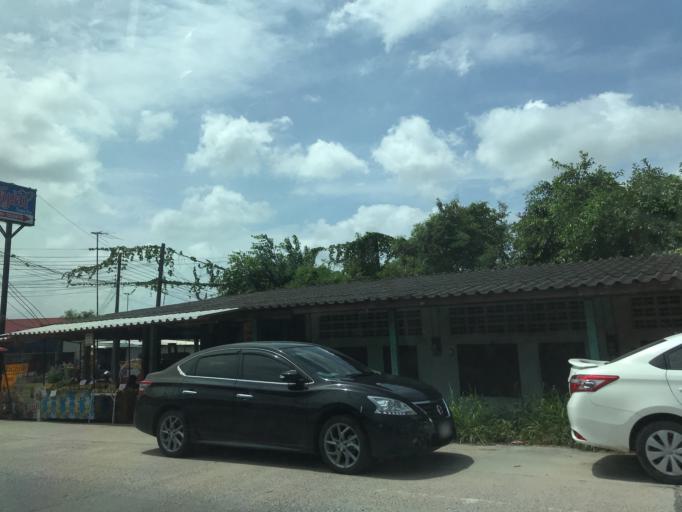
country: TH
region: Chon Buri
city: Si Racha
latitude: 13.1468
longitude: 100.9594
